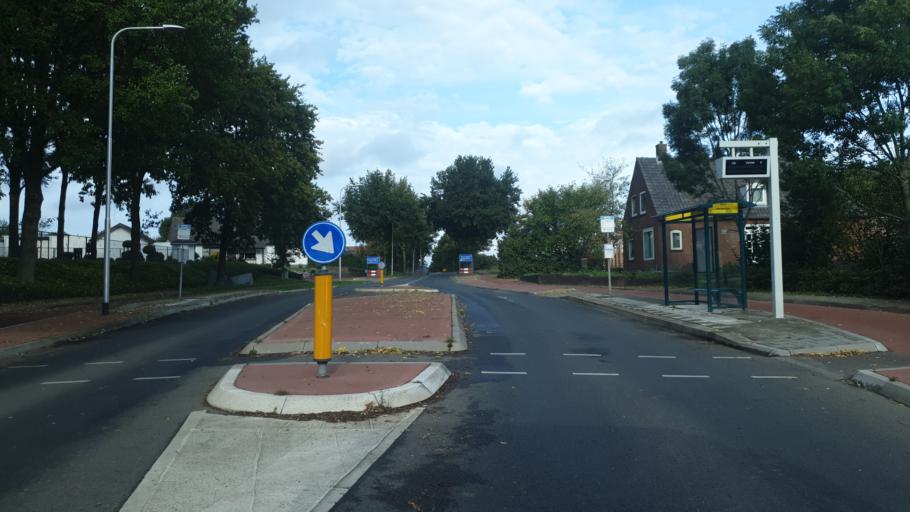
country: NL
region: Gelderland
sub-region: Gemeente Groesbeek
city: Bredeweg
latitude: 51.7626
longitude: 5.9405
